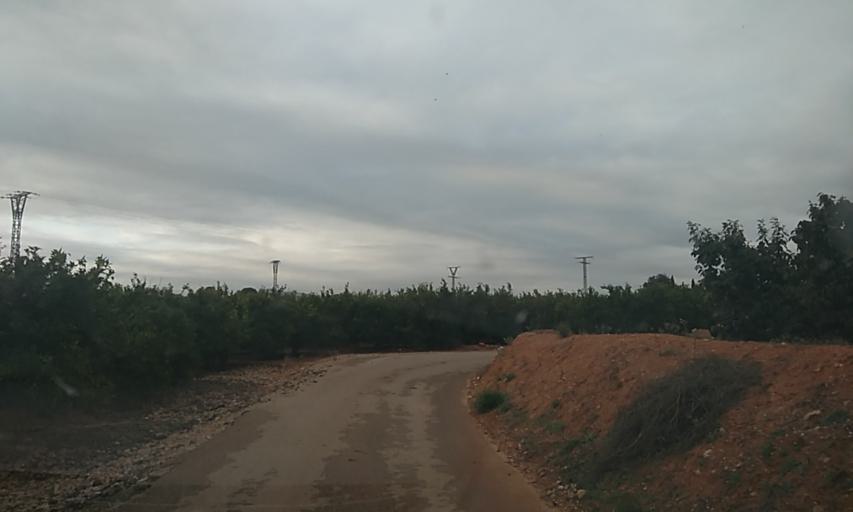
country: ES
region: Valencia
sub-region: Provincia de Valencia
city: Benimodo
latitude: 39.1935
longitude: -0.5665
